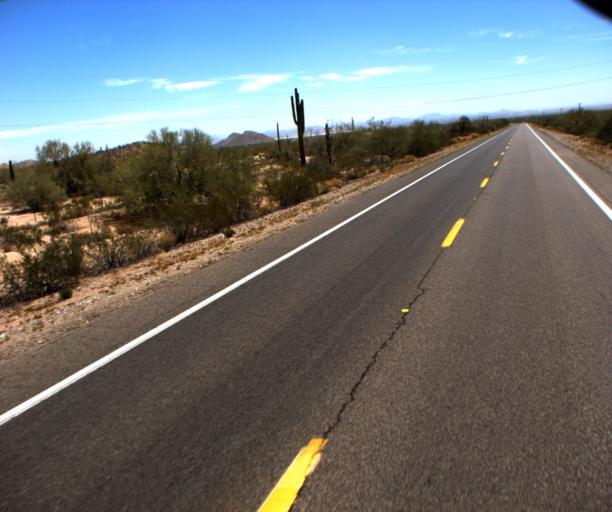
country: US
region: Arizona
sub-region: Pinal County
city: Maricopa
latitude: 32.8409
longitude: -112.1116
